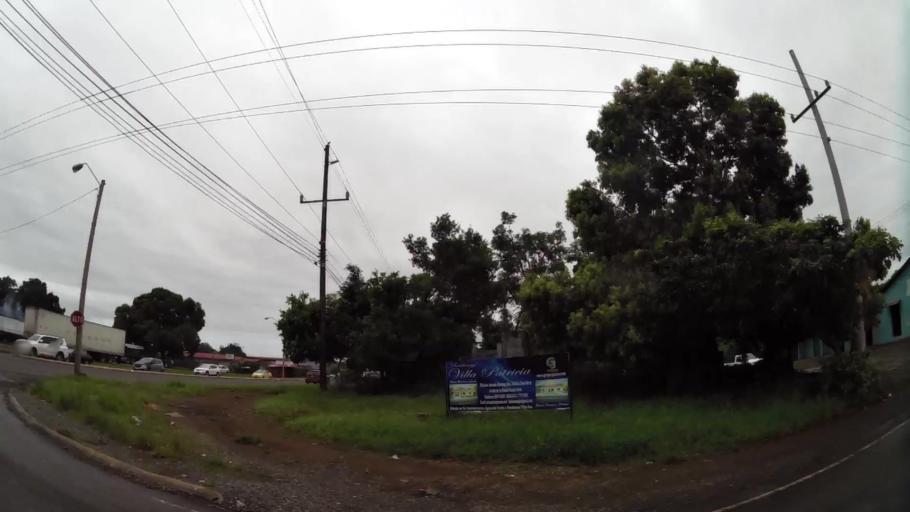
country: PA
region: Chiriqui
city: David
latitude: 8.4332
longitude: -82.4414
